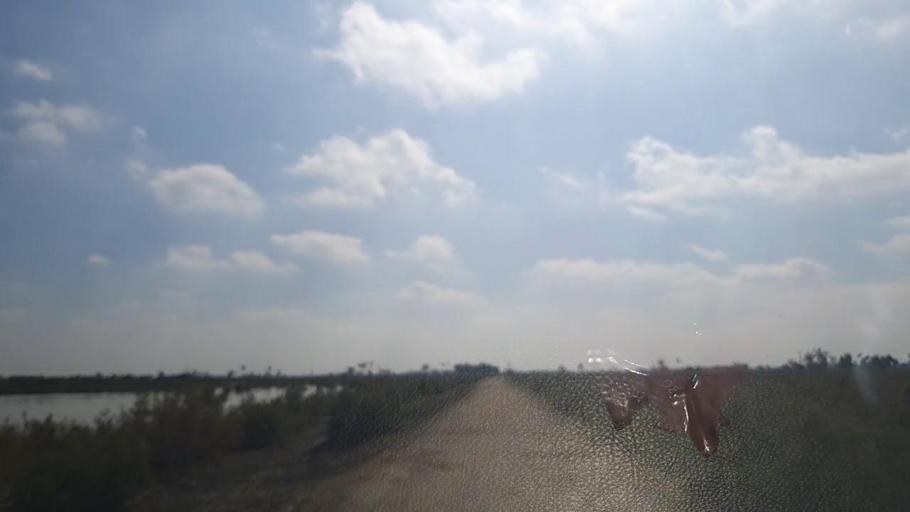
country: PK
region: Sindh
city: Sanghar
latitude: 26.0577
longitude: 69.0056
